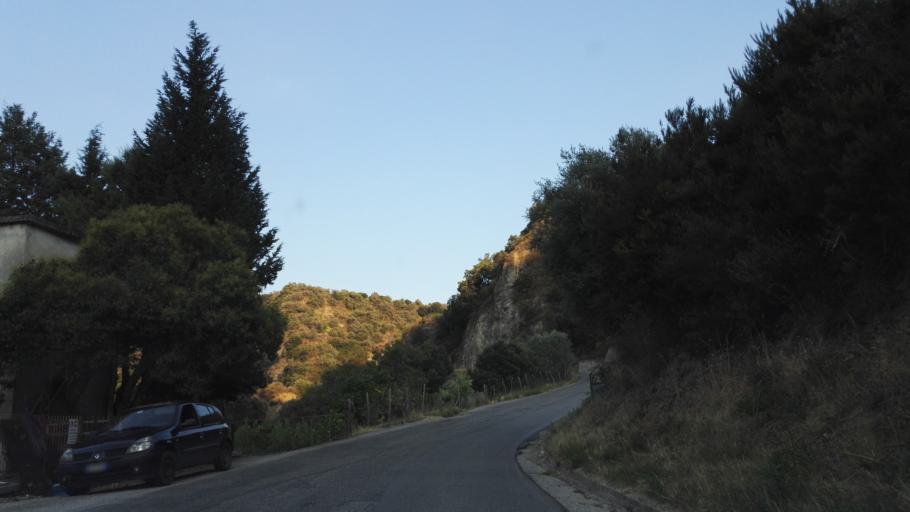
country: IT
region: Calabria
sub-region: Provincia di Reggio Calabria
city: Caulonia
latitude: 38.4010
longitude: 16.4113
